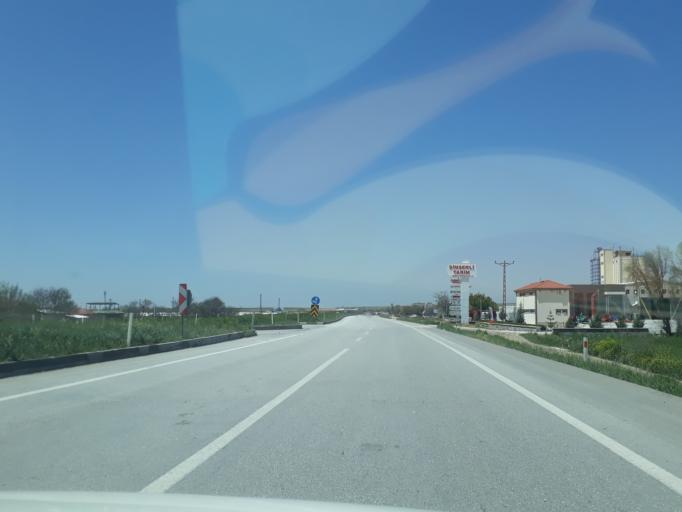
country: TR
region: Konya
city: Karapinar
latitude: 37.7157
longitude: 33.5028
